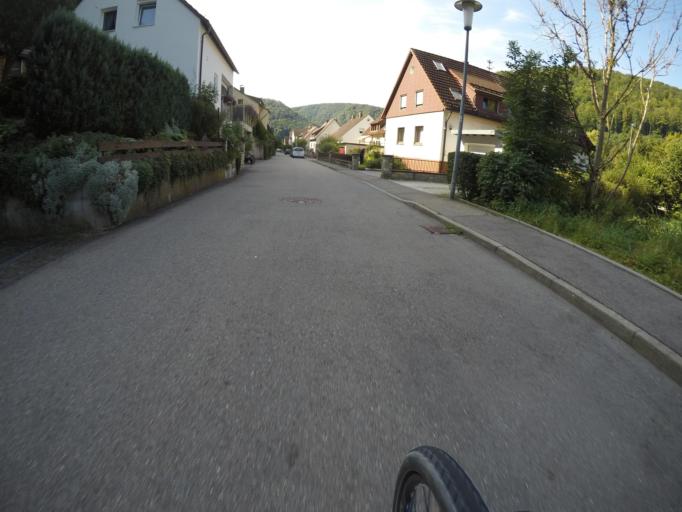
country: DE
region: Baden-Wuerttemberg
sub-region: Regierungsbezirk Stuttgart
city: Geislingen an der Steige
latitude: 48.6416
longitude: 9.8782
